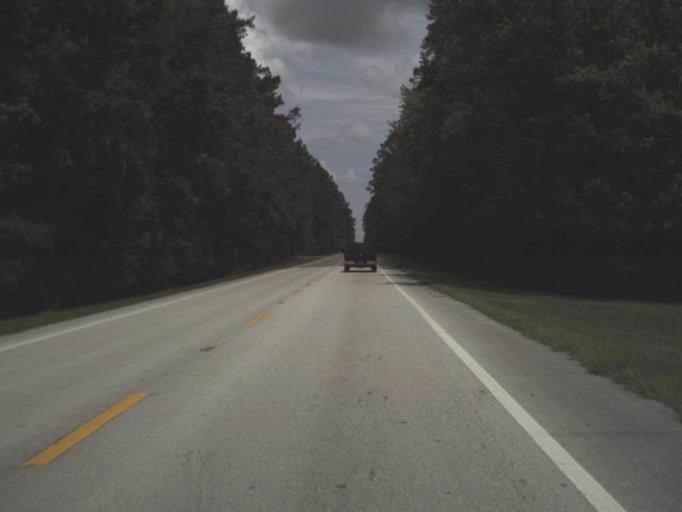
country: US
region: Florida
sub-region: Nassau County
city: Yulee
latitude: 30.6485
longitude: -81.6209
